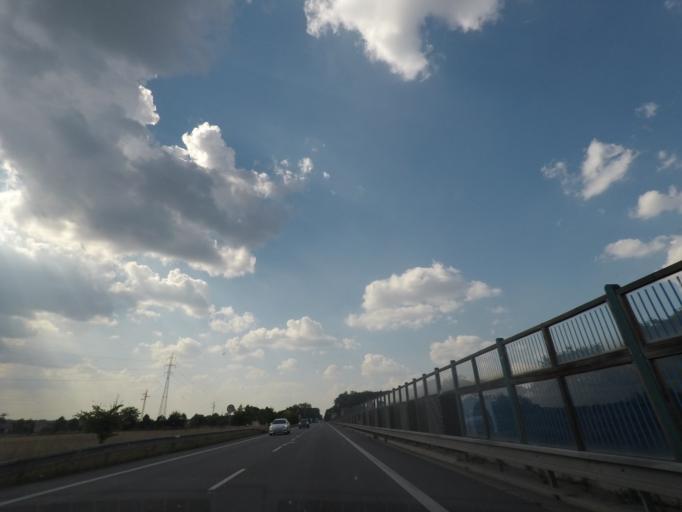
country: CZ
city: Albrechtice nad Orlici
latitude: 50.1712
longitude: 16.0388
